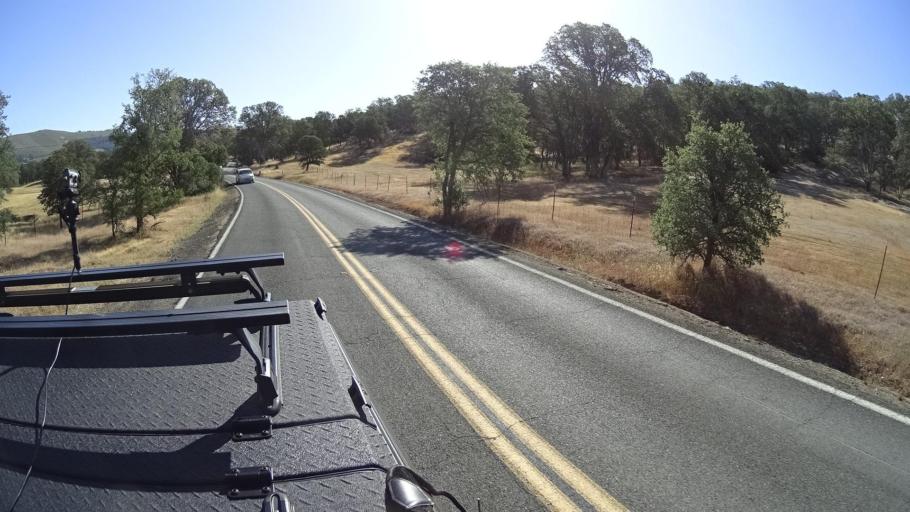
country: US
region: California
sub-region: Lake County
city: Clearlake Oaks
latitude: 39.0058
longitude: -122.6571
